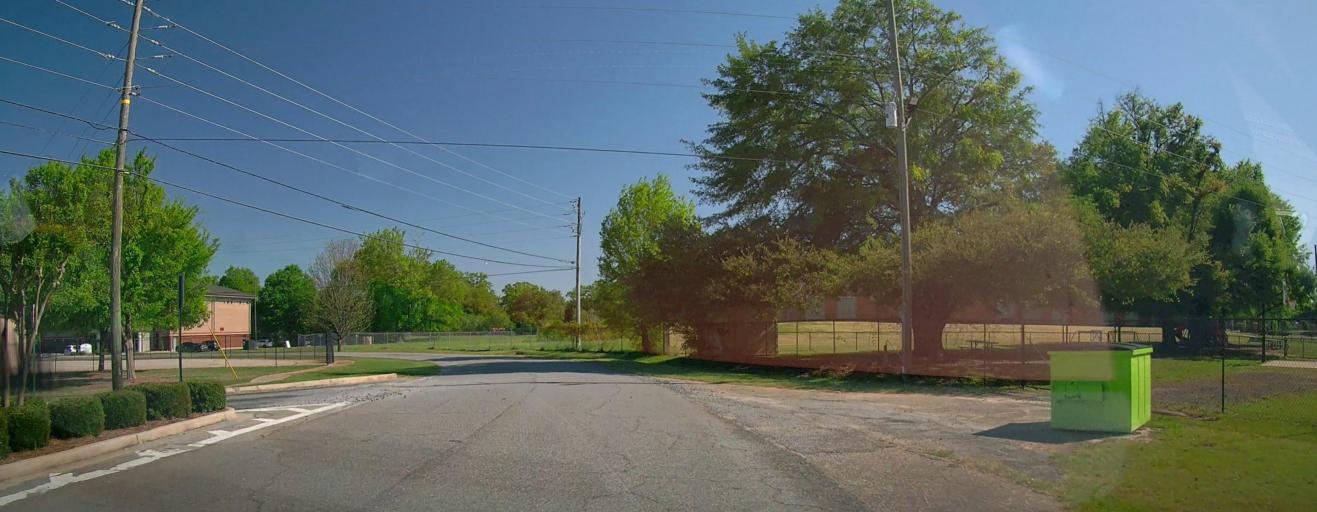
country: US
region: Georgia
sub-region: Houston County
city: Warner Robins
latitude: 32.6168
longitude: -83.6104
